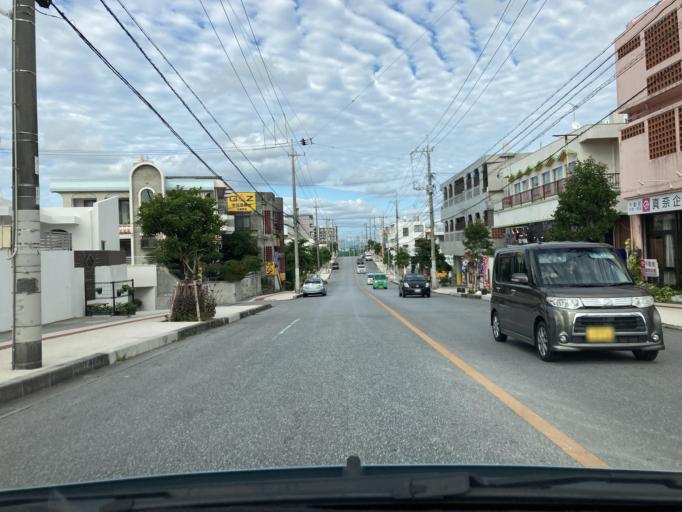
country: JP
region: Okinawa
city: Okinawa
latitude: 26.3363
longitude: 127.8195
